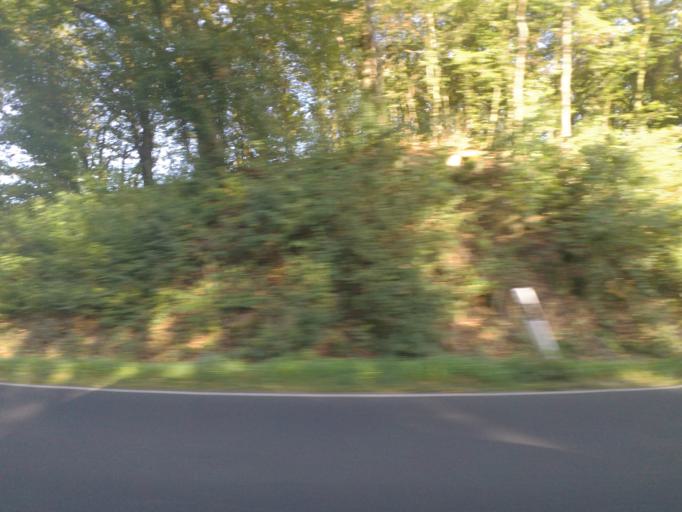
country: DE
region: Hesse
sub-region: Regierungsbezirk Darmstadt
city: Bad Soden-Salmunster
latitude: 50.3294
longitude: 9.3851
